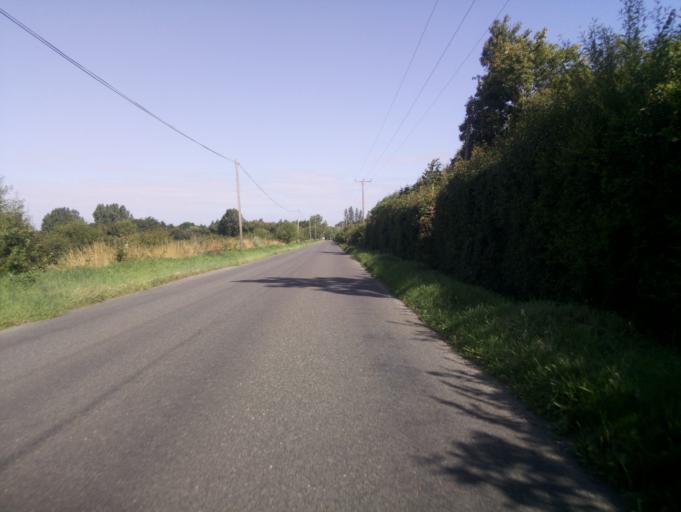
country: GB
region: England
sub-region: Oxfordshire
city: Bampton
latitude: 51.7172
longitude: -1.5294
